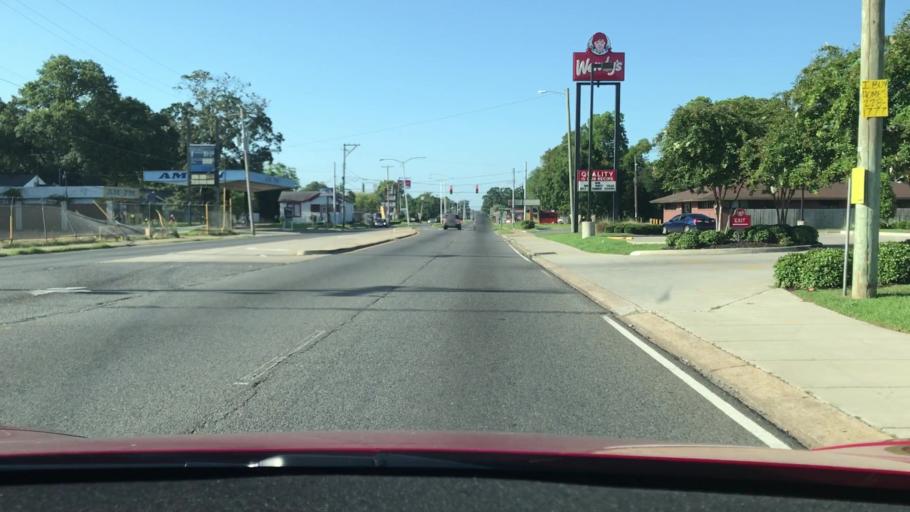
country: US
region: Louisiana
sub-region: Caddo Parish
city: Shreveport
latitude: 32.4775
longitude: -93.7801
